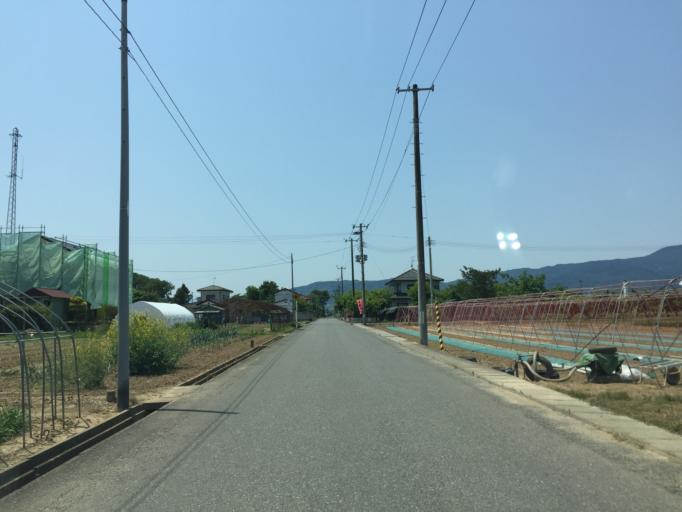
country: JP
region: Fukushima
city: Hobaramachi
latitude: 37.8341
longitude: 140.5566
